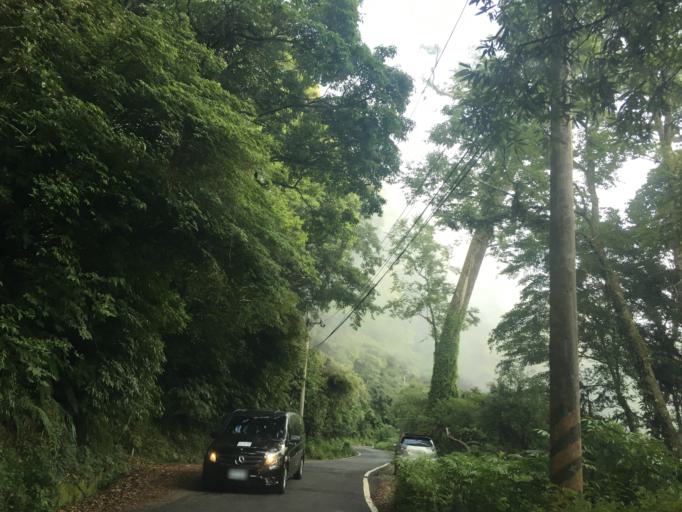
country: TW
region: Taiwan
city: Fengyuan
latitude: 24.2279
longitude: 120.9697
